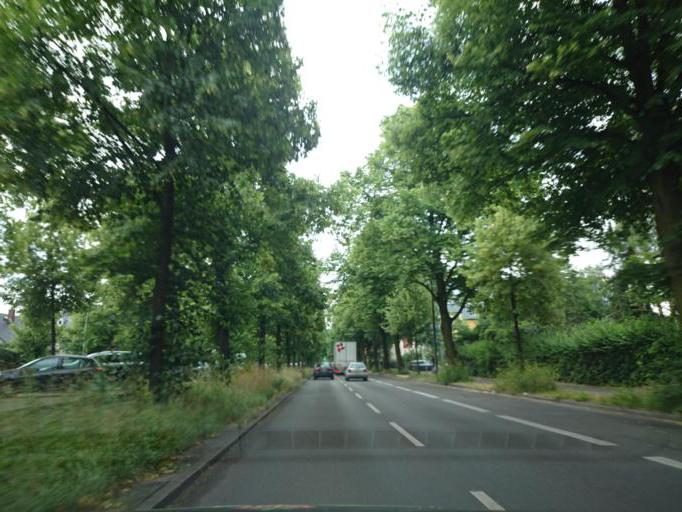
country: DE
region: Berlin
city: Mariendorf
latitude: 52.4225
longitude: 13.3964
